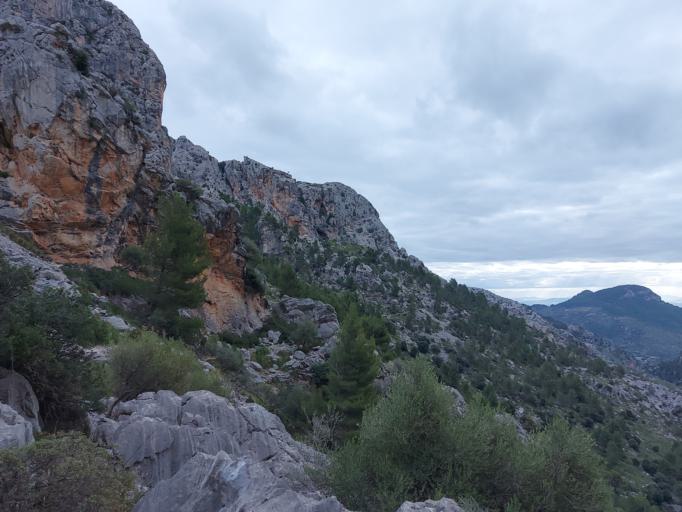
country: ES
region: Balearic Islands
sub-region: Illes Balears
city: Fornalutx
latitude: 39.7745
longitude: 2.8046
